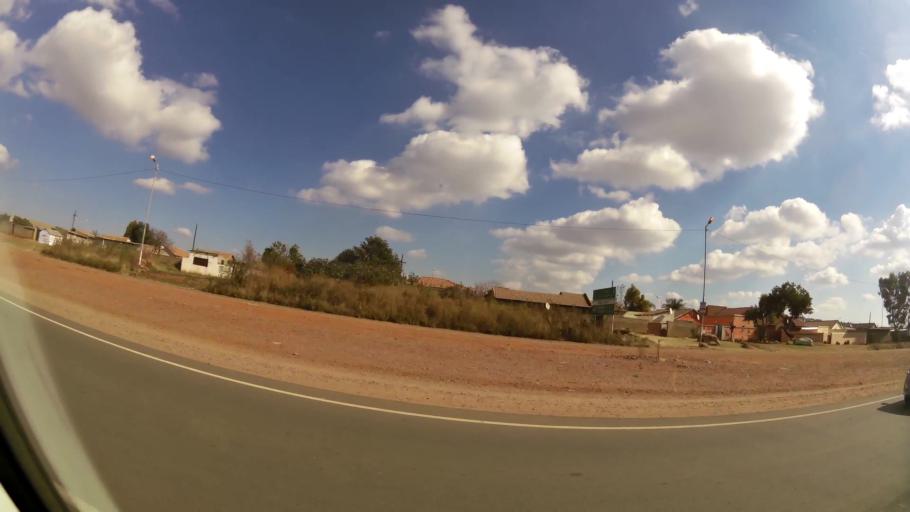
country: ZA
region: Gauteng
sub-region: City of Tshwane Metropolitan Municipality
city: Cullinan
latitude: -25.7013
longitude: 28.4193
